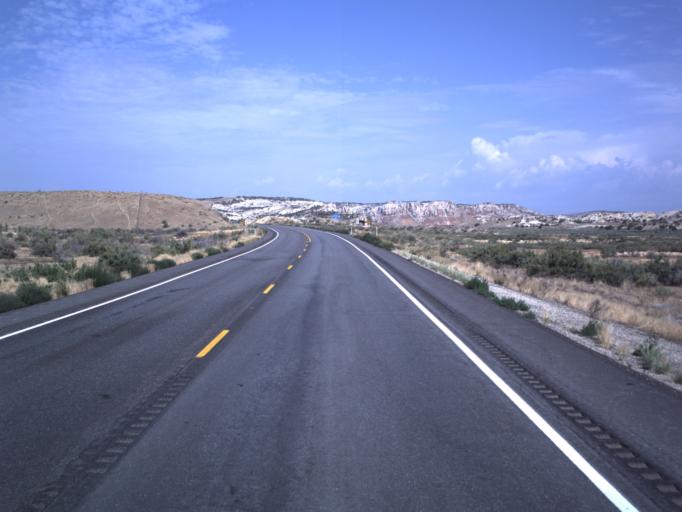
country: US
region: Utah
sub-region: Uintah County
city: Naples
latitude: 40.3137
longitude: -109.2266
